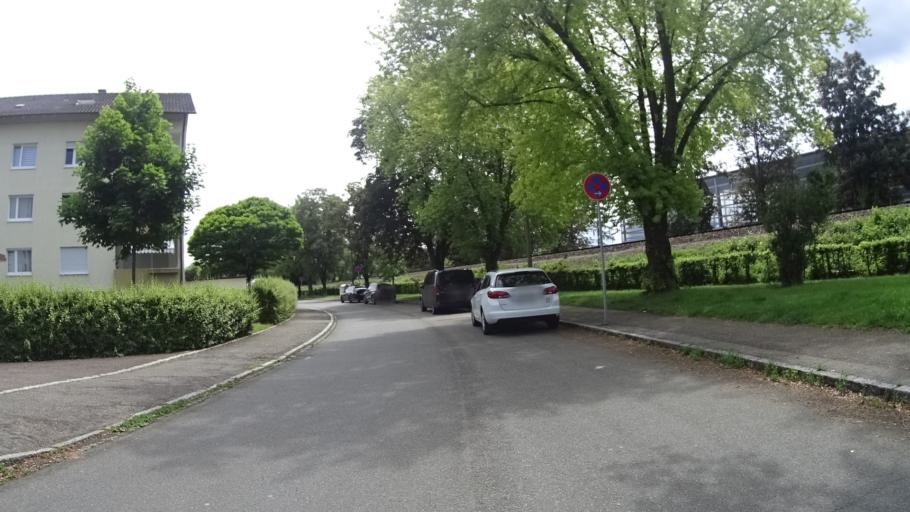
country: CH
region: Basel-City
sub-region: Basel-Stadt
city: Bettingen
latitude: 47.5542
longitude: 7.6488
